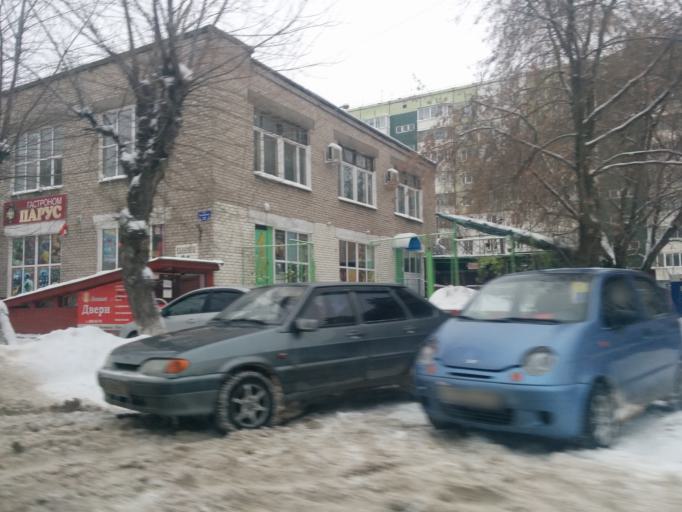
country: RU
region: Perm
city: Kondratovo
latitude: 58.0266
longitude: 56.0157
